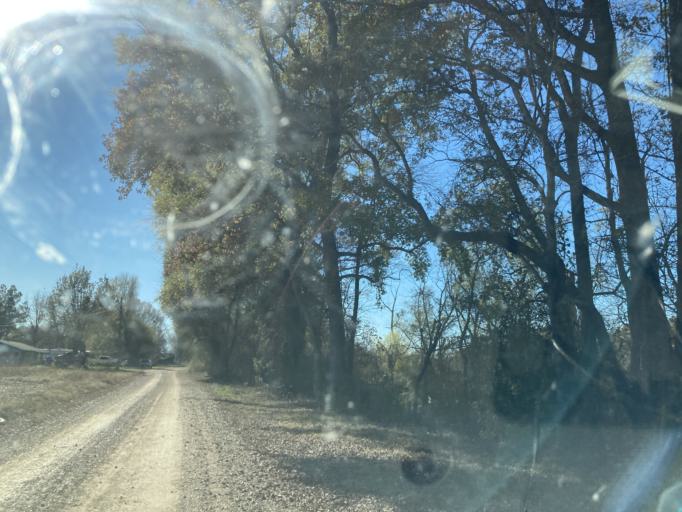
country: US
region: Mississippi
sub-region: Sharkey County
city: Rolling Fork
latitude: 32.7522
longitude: -90.6940
